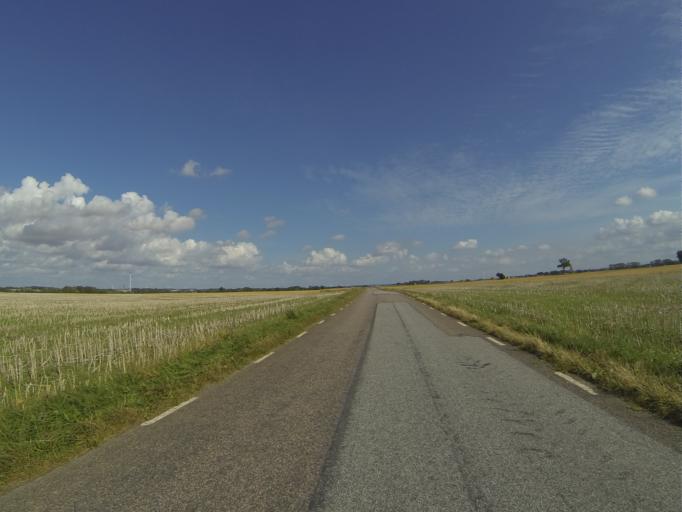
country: SE
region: Skane
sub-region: Kavlinge Kommun
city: Kaevlinge
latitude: 55.7848
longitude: 13.1455
